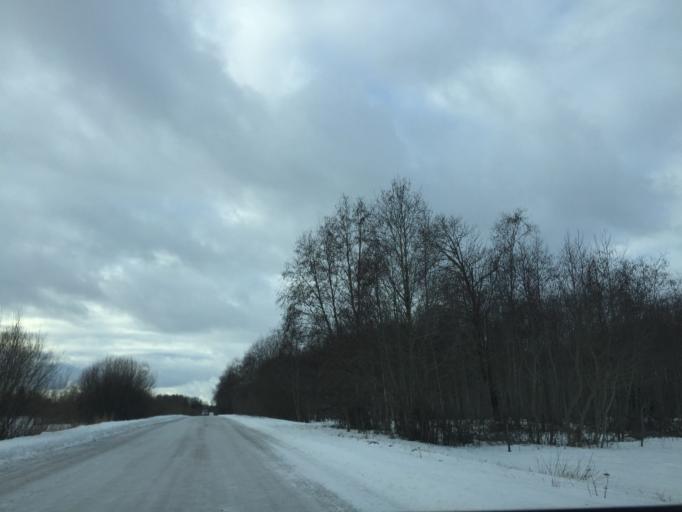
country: LV
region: Lielvarde
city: Lielvarde
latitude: 56.6051
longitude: 24.7516
